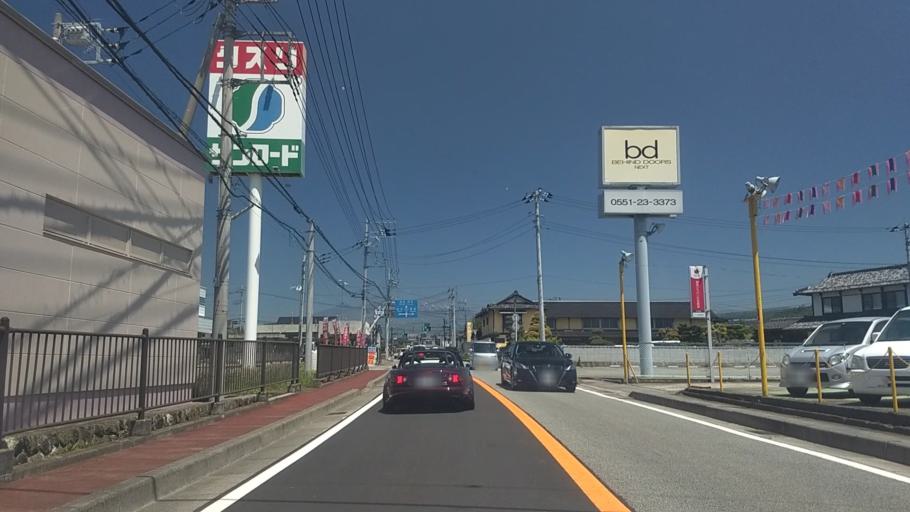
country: JP
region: Yamanashi
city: Nirasaki
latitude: 35.7275
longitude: 138.4491
